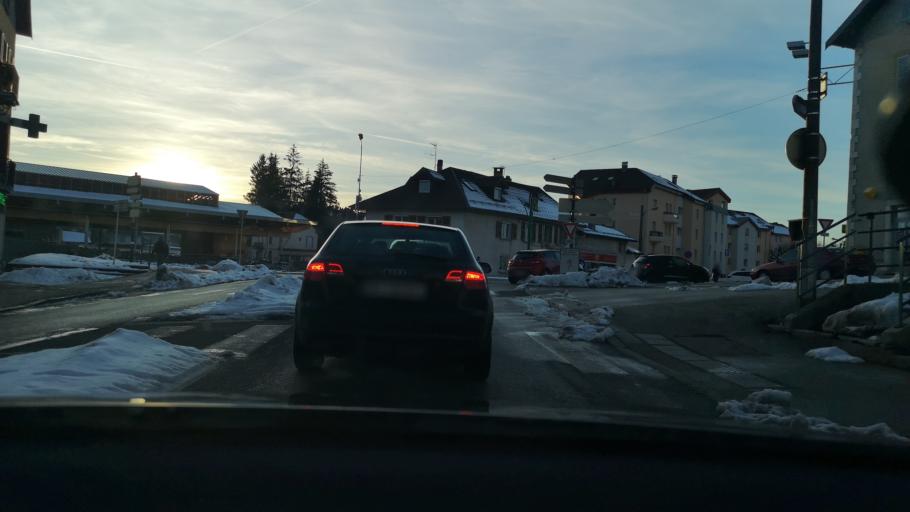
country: FR
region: Franche-Comte
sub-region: Departement du Doubs
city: Pontarlier
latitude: 46.9058
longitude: 6.3582
